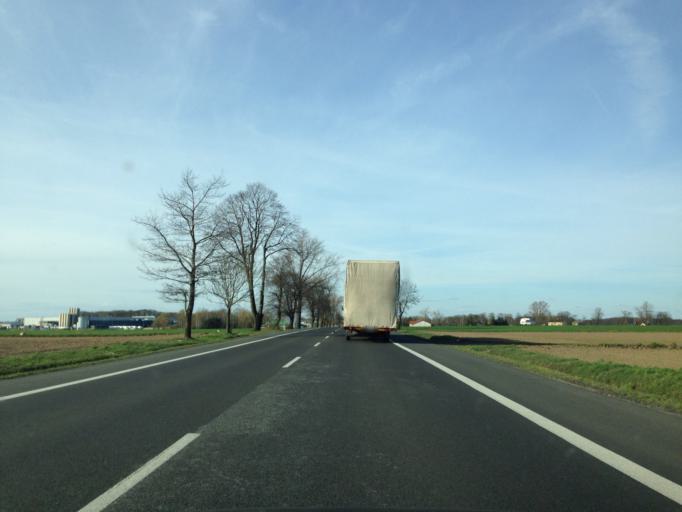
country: PL
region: Kujawsko-Pomorskie
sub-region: Powiat wloclawski
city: Lubien Kujawski
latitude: 52.3913
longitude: 19.1700
